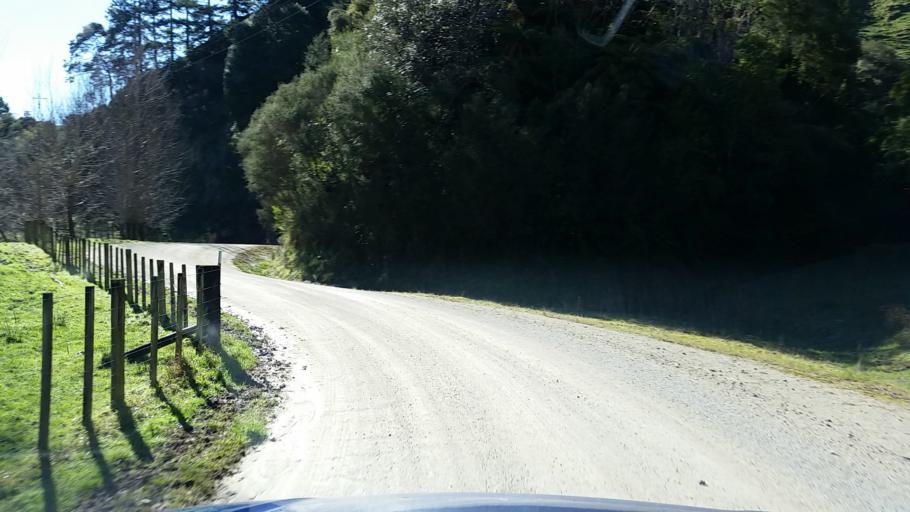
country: NZ
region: Manawatu-Wanganui
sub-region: Wanganui District
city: Wanganui
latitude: -39.5509
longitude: 174.8964
